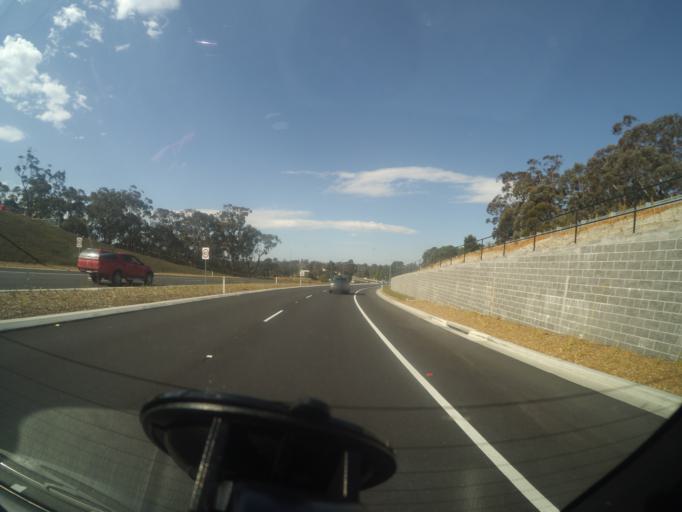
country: AU
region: New South Wales
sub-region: Blue Mountains Municipality
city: Lawson
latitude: -33.7242
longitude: 150.4056
